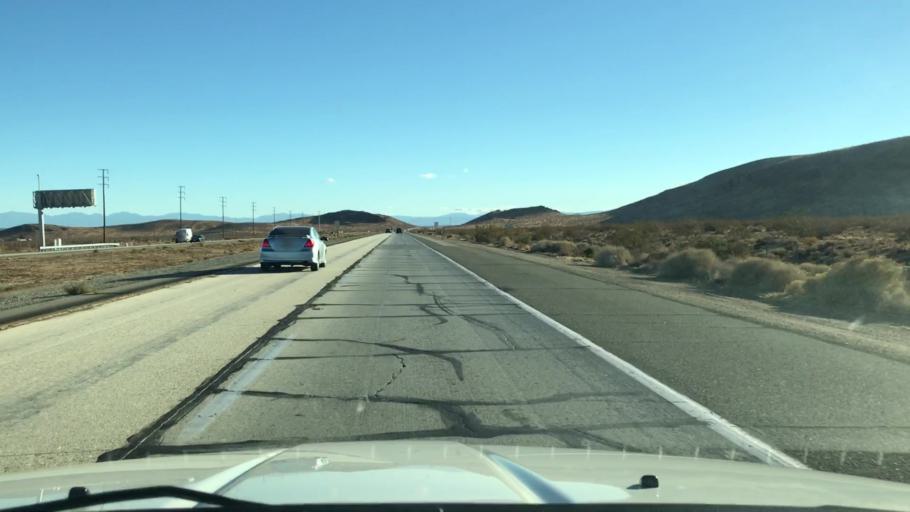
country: US
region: California
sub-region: Kern County
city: Mojave
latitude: 34.9884
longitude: -118.1595
